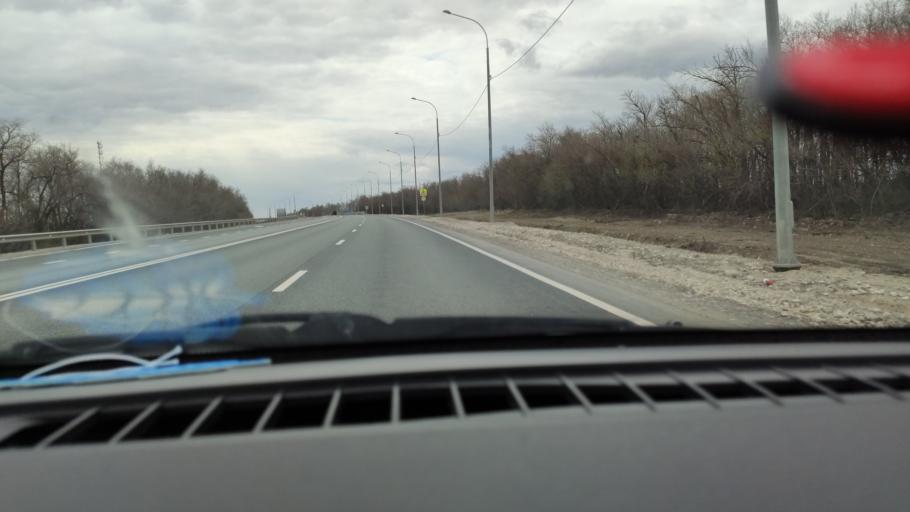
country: RU
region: Saratov
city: Yelshanka
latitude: 51.8935
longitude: 46.5274
